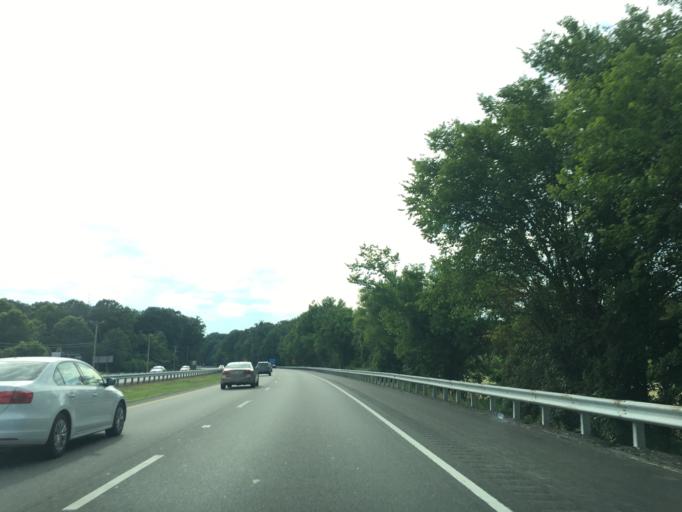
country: US
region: Maryland
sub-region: Queen Anne's County
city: Grasonville
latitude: 38.9810
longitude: -76.1430
